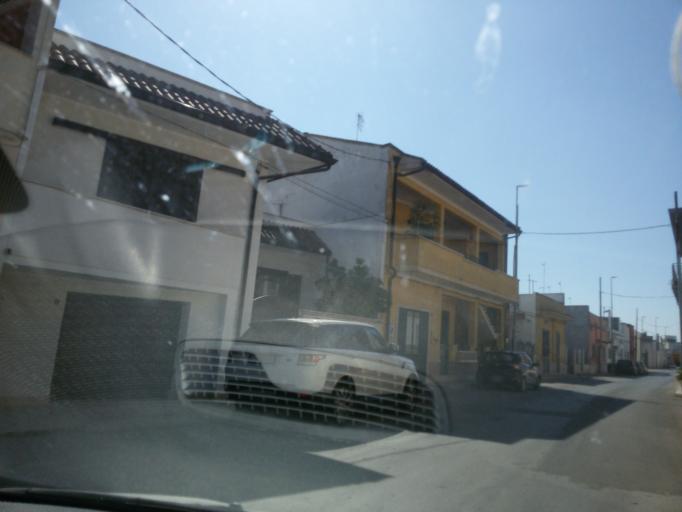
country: IT
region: Apulia
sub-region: Provincia di Brindisi
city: San Donaci
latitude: 40.4451
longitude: 17.9261
